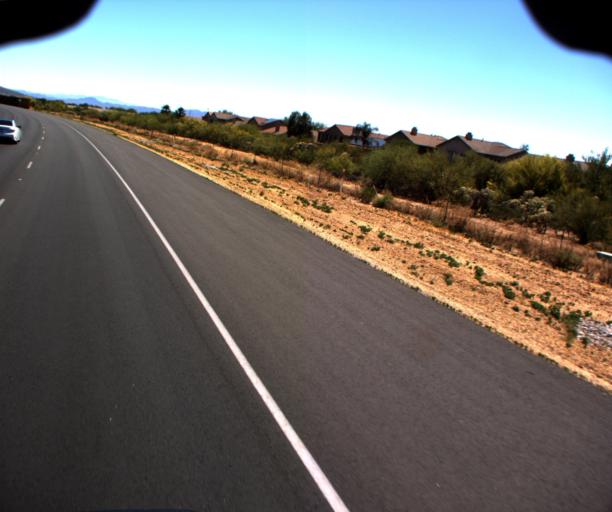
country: US
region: Arizona
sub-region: Pima County
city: Catalina
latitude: 32.4523
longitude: -110.9331
